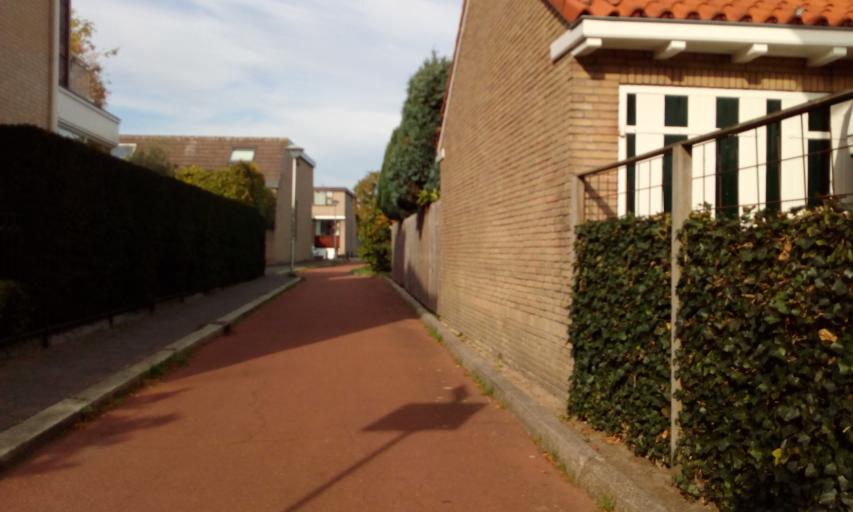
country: NL
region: South Holland
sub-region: Gemeente Wassenaar
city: Wassenaar
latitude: 52.1410
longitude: 4.3913
